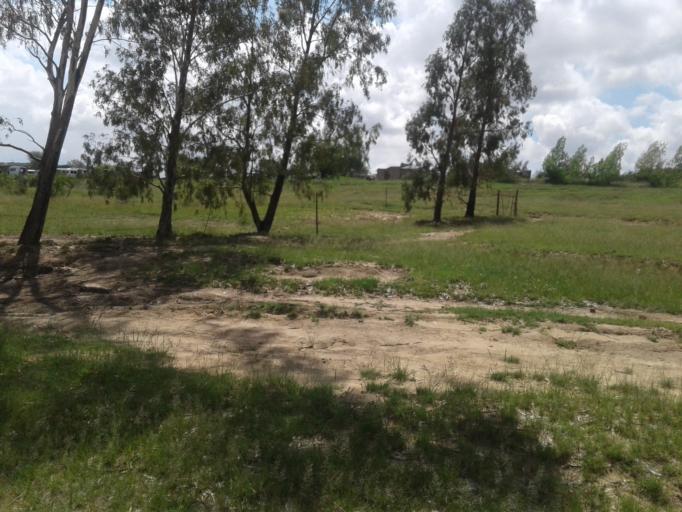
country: LS
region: Mafeteng
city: Mafeteng
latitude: -29.7492
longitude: 27.1122
